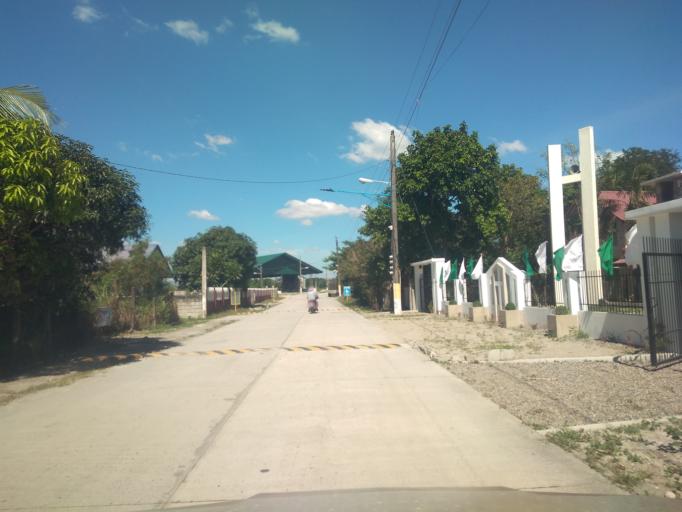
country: PH
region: Central Luzon
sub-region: Province of Pampanga
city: Balas
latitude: 15.0508
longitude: 120.6113
